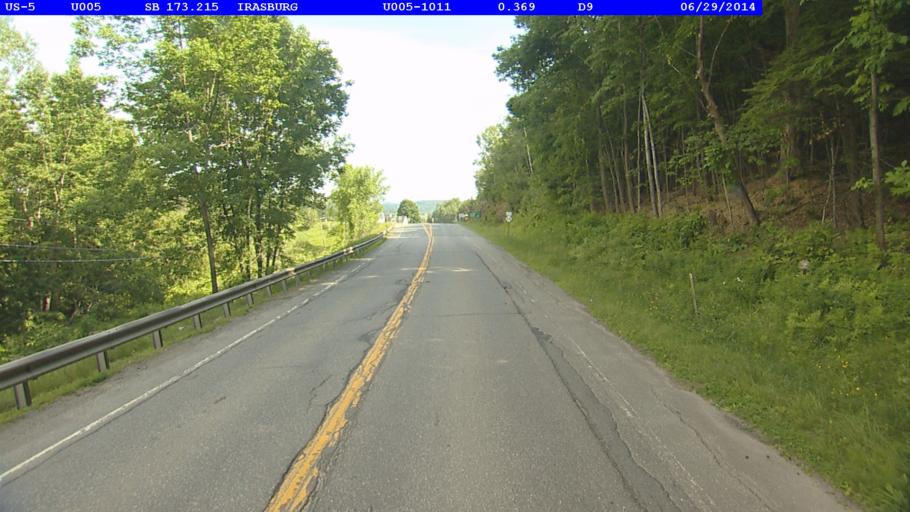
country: US
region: Vermont
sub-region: Orleans County
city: Newport
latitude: 44.8113
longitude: -72.2174
